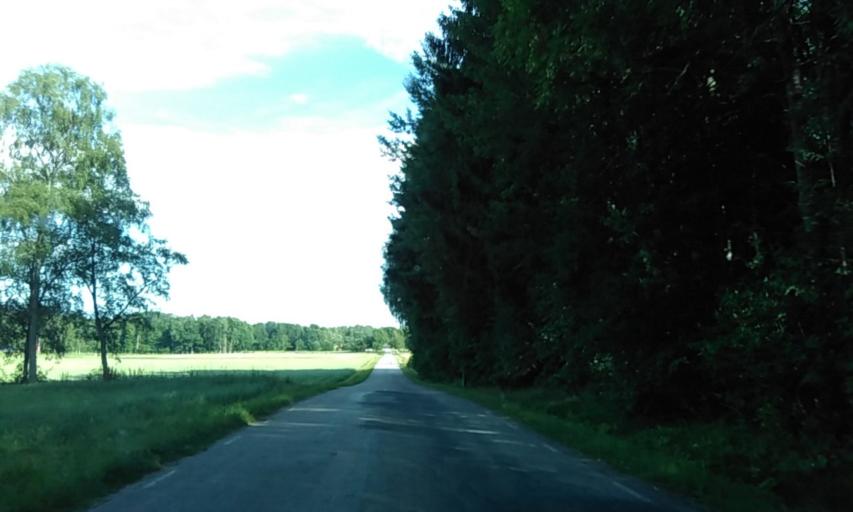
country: SE
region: Vaestra Goetaland
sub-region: Vara Kommun
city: Vara
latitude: 58.3675
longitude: 12.8577
